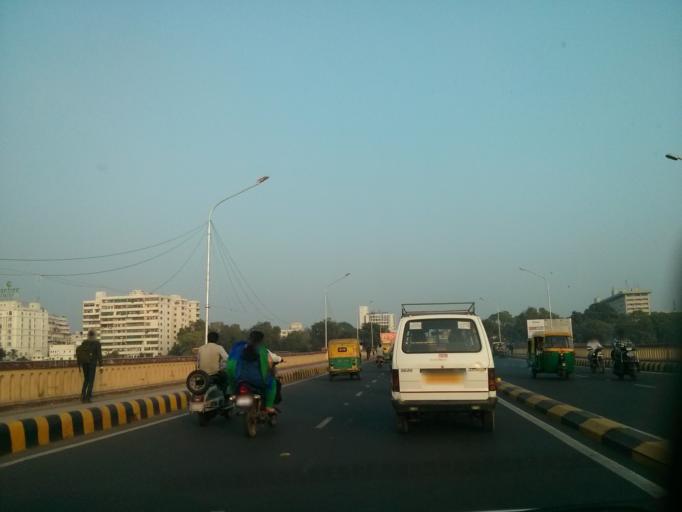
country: IN
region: Gujarat
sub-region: Ahmadabad
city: Ahmedabad
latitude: 23.0270
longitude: 72.5743
